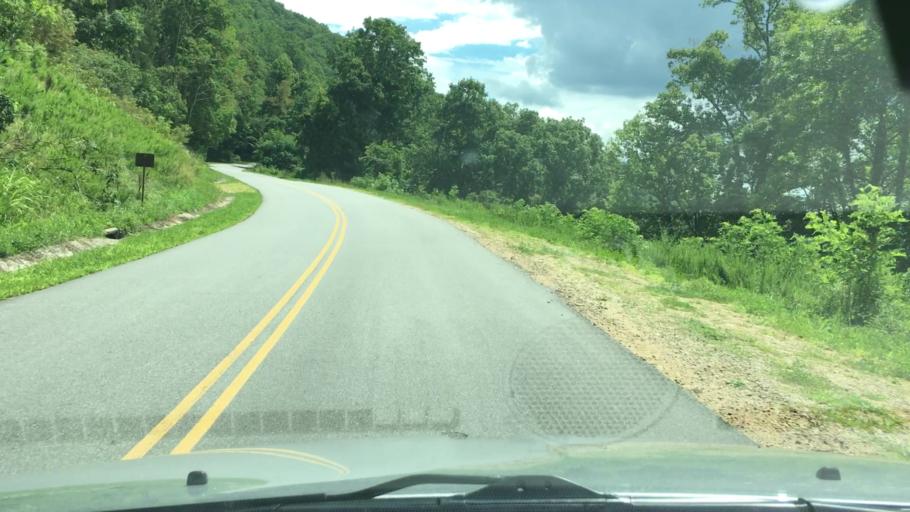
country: US
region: North Carolina
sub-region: Buncombe County
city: Swannanoa
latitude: 35.6625
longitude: -82.4607
